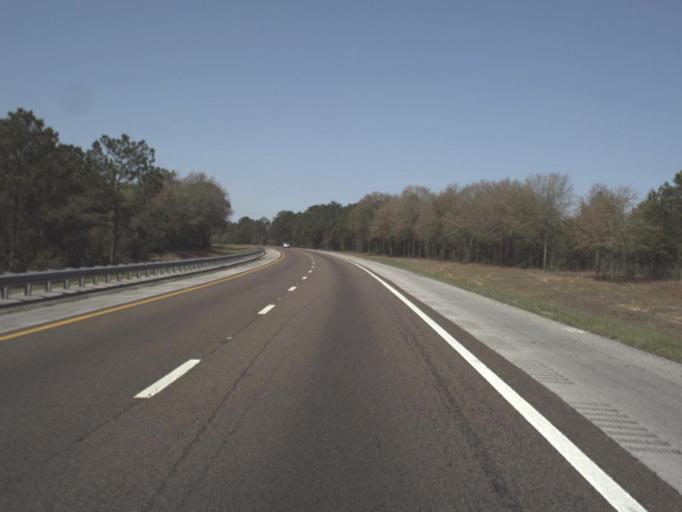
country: US
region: Florida
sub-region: Walton County
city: DeFuniak Springs
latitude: 30.7509
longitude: -86.2818
